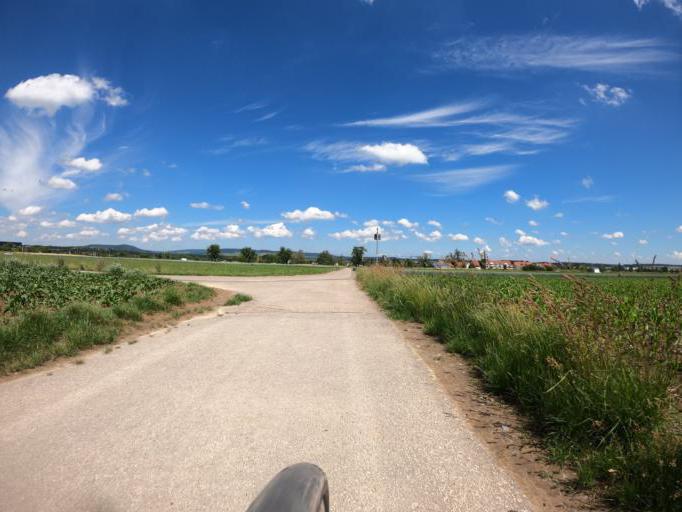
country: DE
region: Baden-Wuerttemberg
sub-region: Regierungsbezirk Stuttgart
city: Oberriexingen
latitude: 48.9500
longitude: 9.0590
